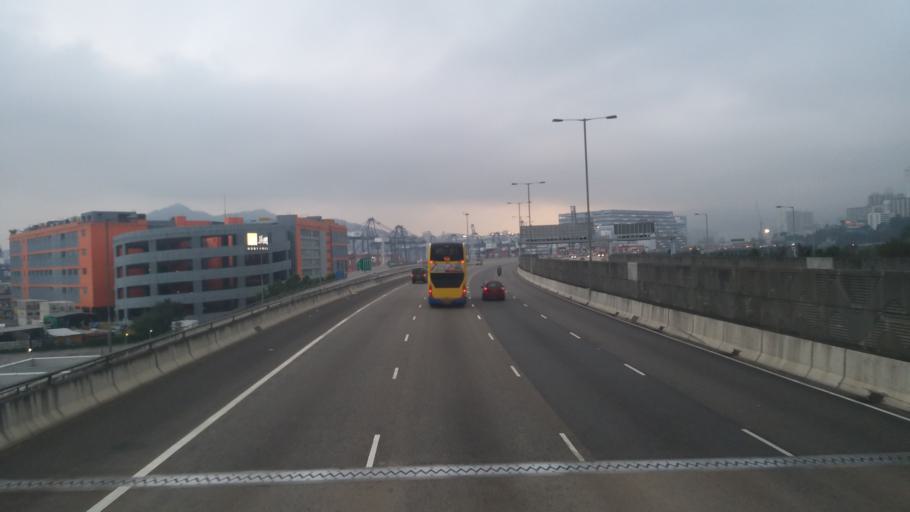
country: HK
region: Sham Shui Po
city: Sham Shui Po
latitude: 22.3339
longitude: 114.1370
